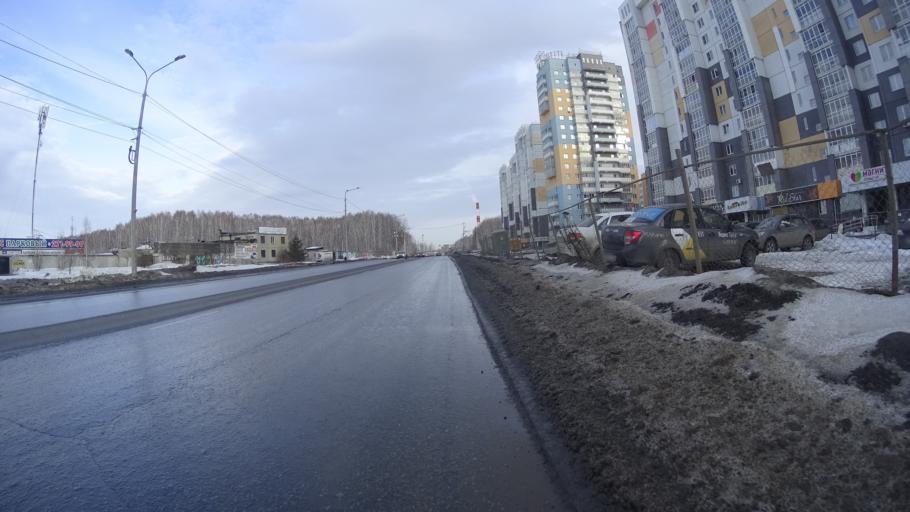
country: RU
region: Chelyabinsk
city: Roshchino
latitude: 55.2087
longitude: 61.3035
